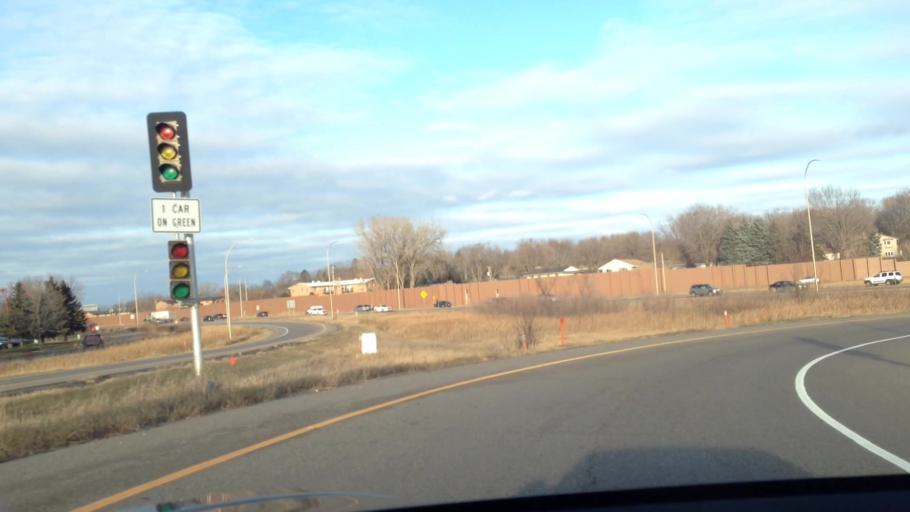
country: US
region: Minnesota
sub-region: Hennepin County
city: New Hope
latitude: 45.0344
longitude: -93.4022
